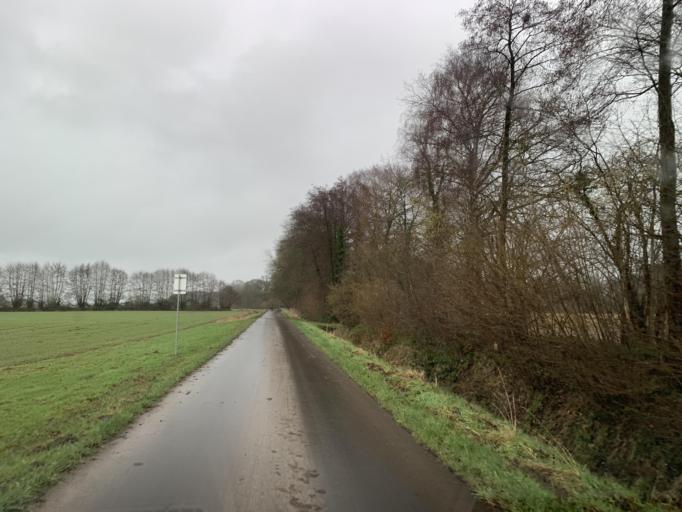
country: DE
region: North Rhine-Westphalia
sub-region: Regierungsbezirk Munster
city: Havixbeck
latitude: 51.9448
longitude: 7.4945
